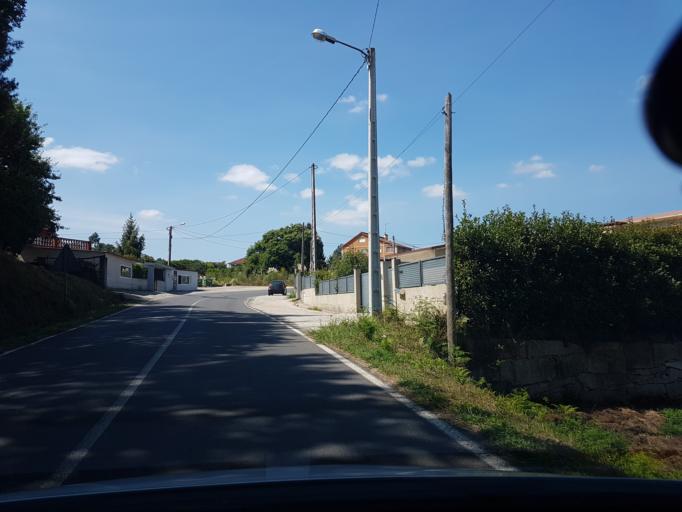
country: ES
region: Galicia
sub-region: Provincia de Pontevedra
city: Porrino
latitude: 42.2051
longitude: -8.6225
